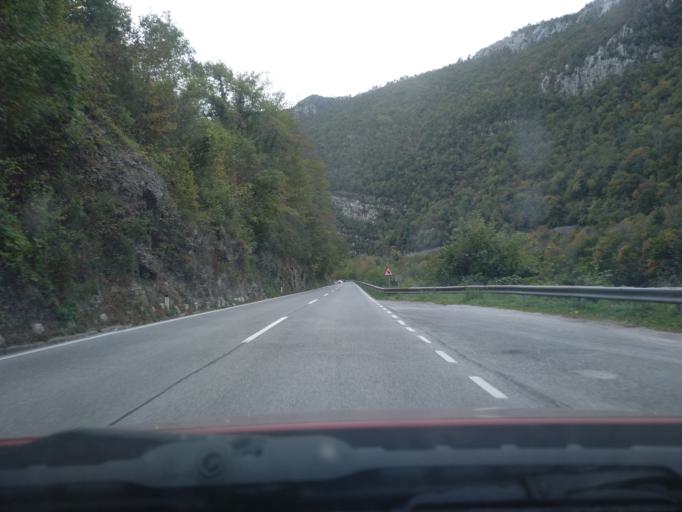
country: SI
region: Kanal
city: Deskle
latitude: 46.0135
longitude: 13.6125
